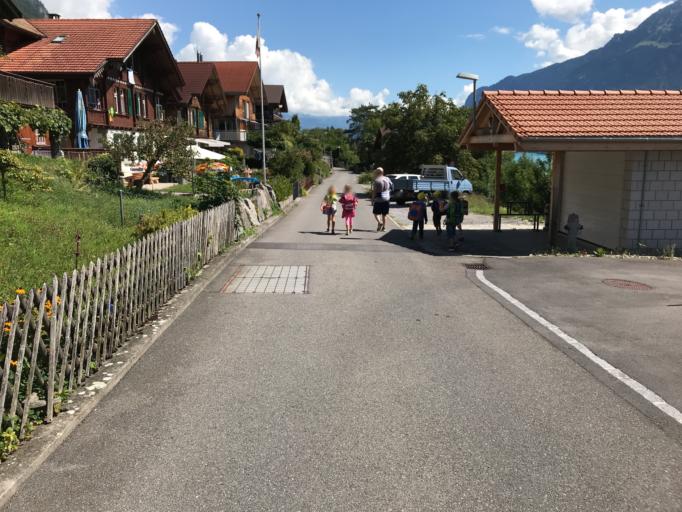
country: CH
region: Bern
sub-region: Interlaken-Oberhasli District
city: Ringgenberg
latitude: 46.7029
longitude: 7.8987
